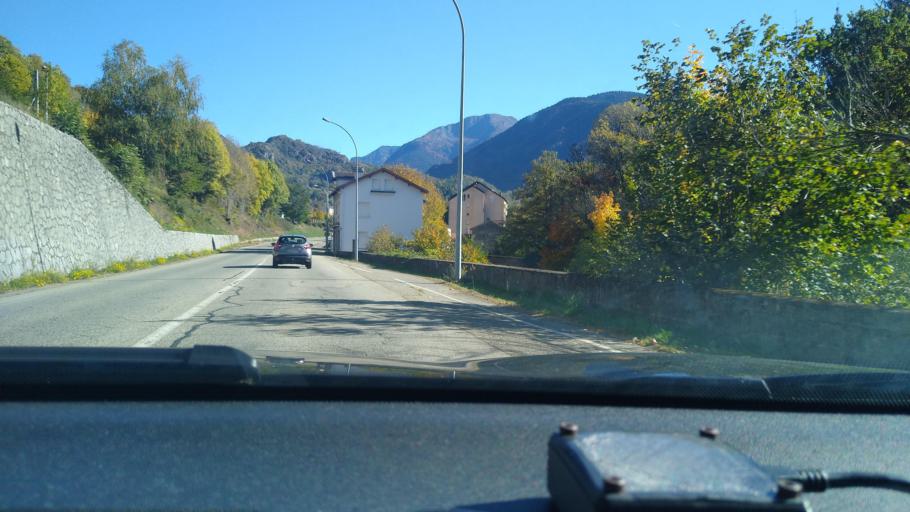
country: FR
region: Midi-Pyrenees
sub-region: Departement de l'Ariege
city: Ax-les-Thermes
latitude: 42.7277
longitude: 1.8282
